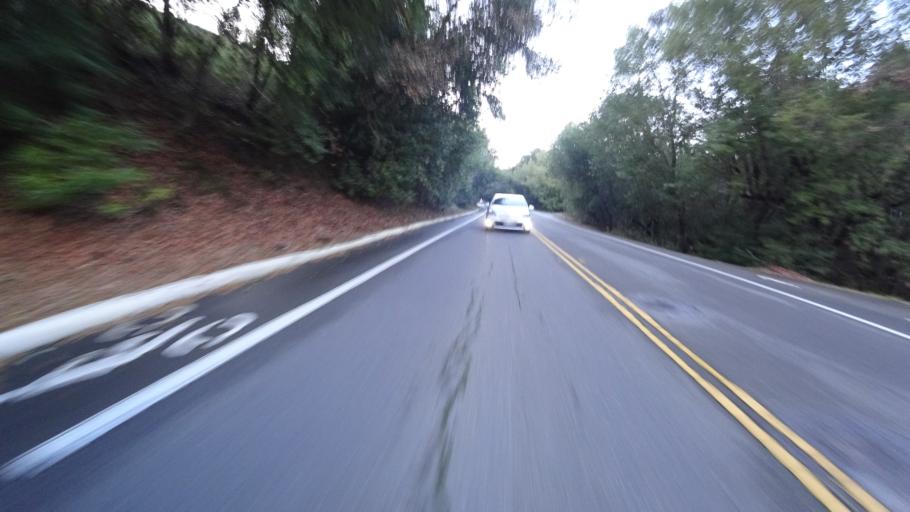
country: US
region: California
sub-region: Alameda County
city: Dublin
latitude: 37.6953
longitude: -121.9497
